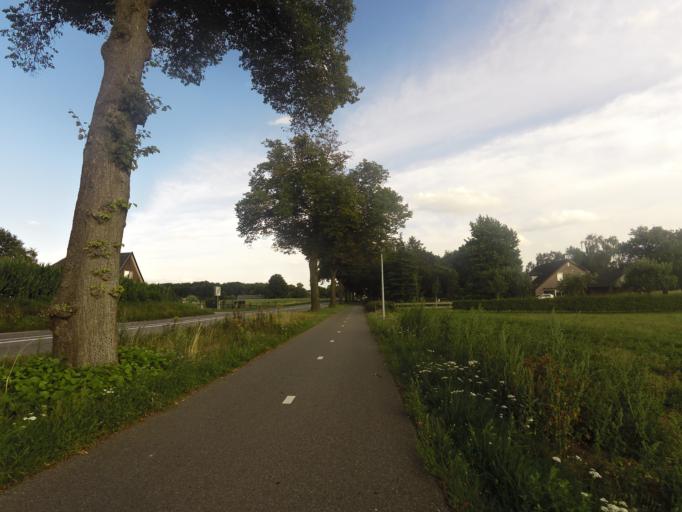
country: NL
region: Gelderland
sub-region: Gemeente Doetinchem
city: Doetinchem
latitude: 51.9386
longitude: 6.3205
